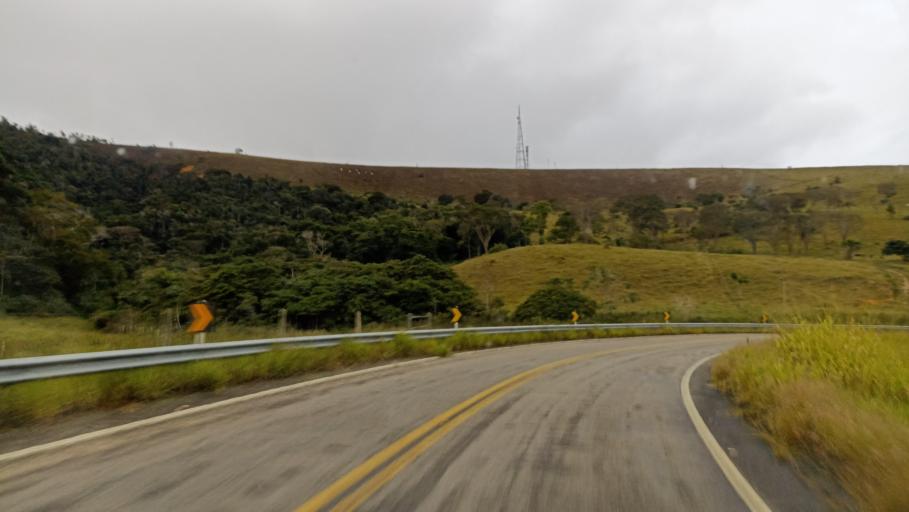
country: BR
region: Minas Gerais
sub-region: Joaima
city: Joaima
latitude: -16.6808
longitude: -40.5214
